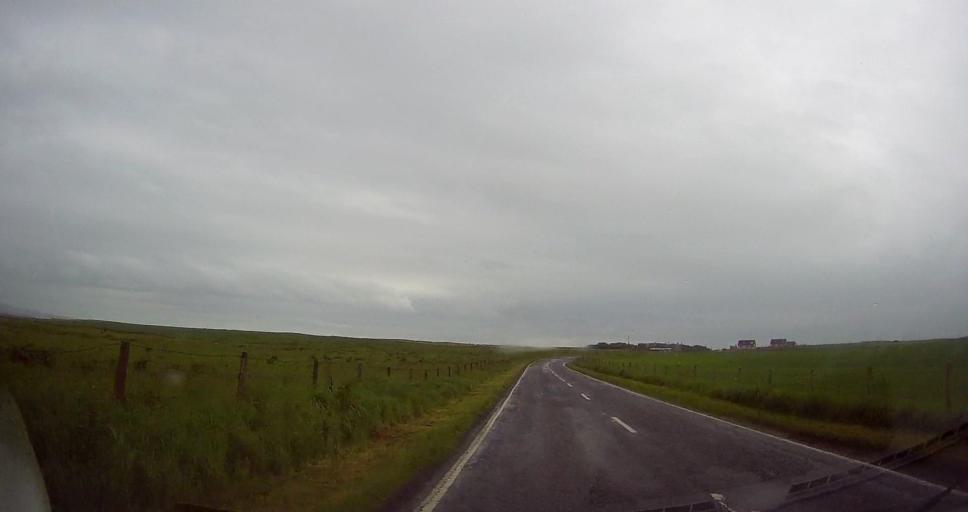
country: GB
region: Scotland
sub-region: Orkney Islands
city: Stromness
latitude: 59.0569
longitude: -3.2815
